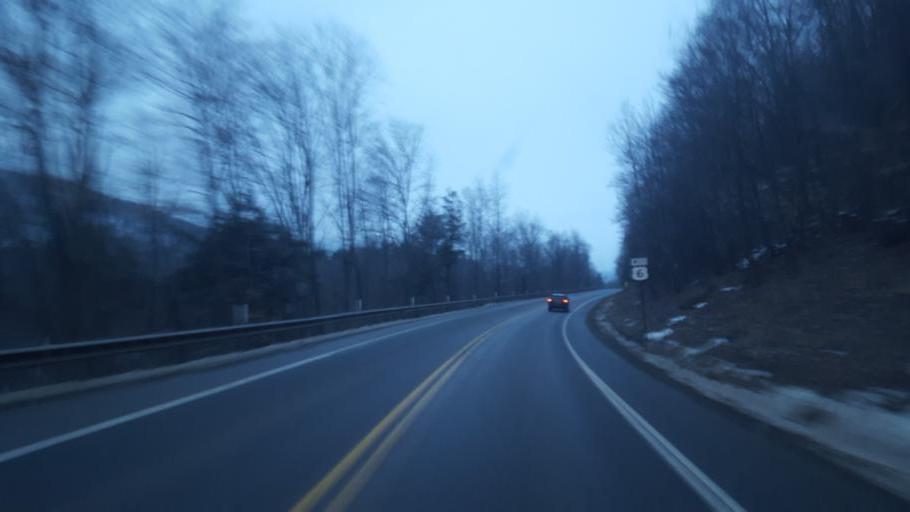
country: US
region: Pennsylvania
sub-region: Potter County
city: Coudersport
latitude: 41.7530
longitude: -78.1052
